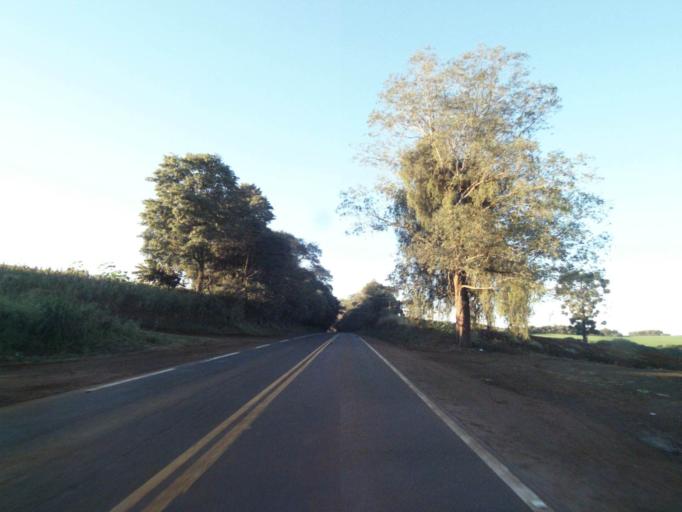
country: BR
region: Parana
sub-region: Faxinal
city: Faxinal
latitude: -23.7634
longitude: -51.1417
